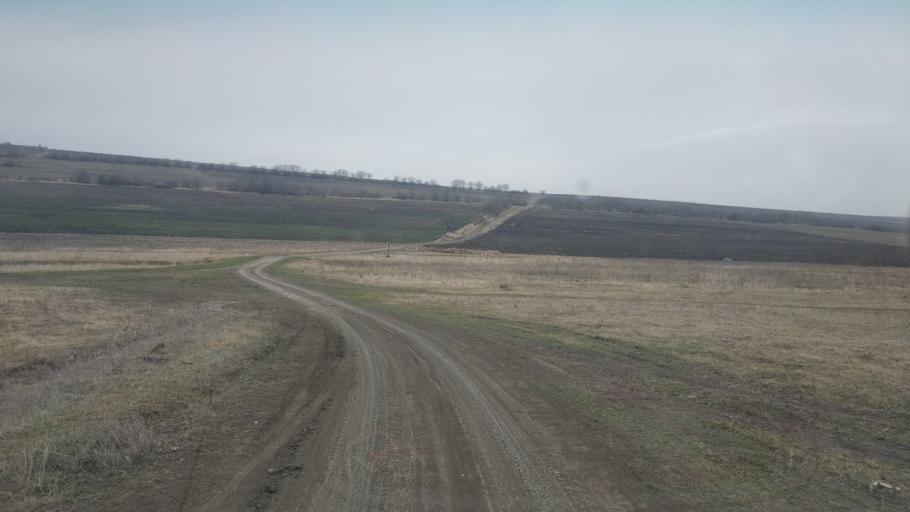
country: MD
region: Chisinau
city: Singera
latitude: 46.8272
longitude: 29.0128
